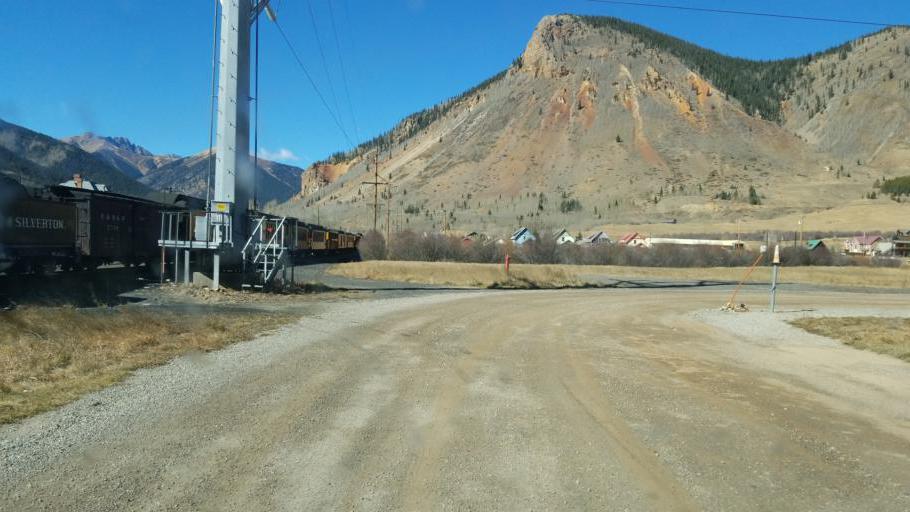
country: US
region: Colorado
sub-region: San Juan County
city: Silverton
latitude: 37.8046
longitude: -107.6676
